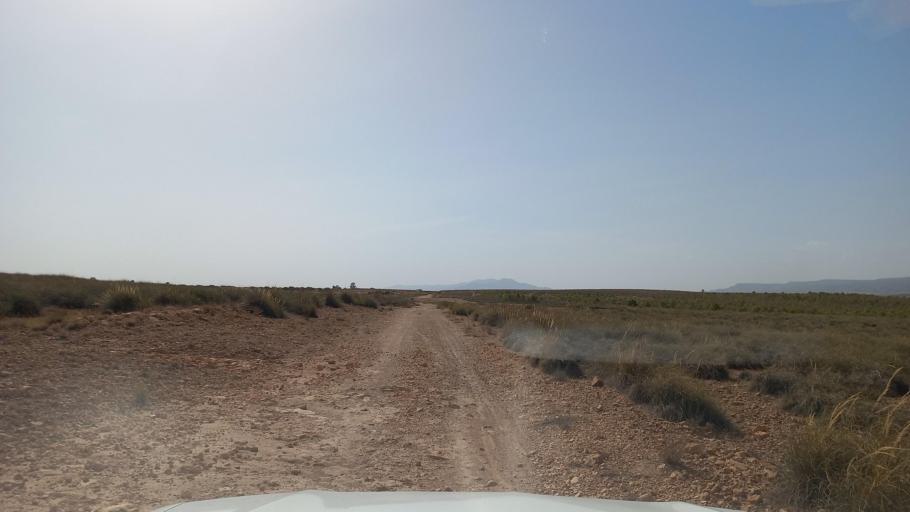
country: TN
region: Al Qasrayn
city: Kasserine
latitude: 35.2152
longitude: 8.9843
